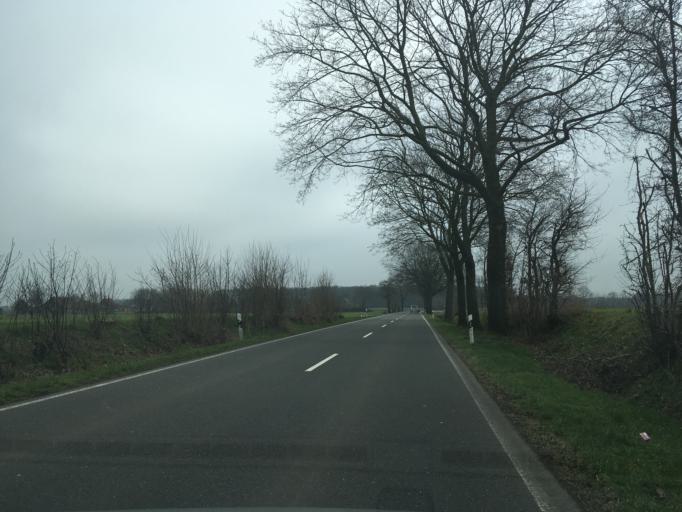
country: DE
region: North Rhine-Westphalia
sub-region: Regierungsbezirk Munster
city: Rhede
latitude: 51.8636
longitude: 6.7411
